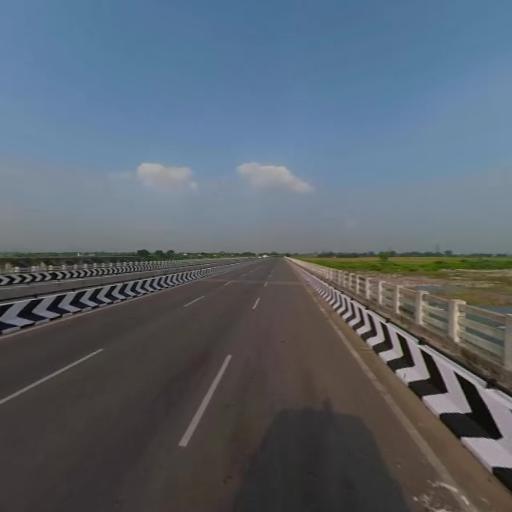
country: IN
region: Telangana
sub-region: Nalgonda
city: Suriapet
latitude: 17.1639
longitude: 79.5215
